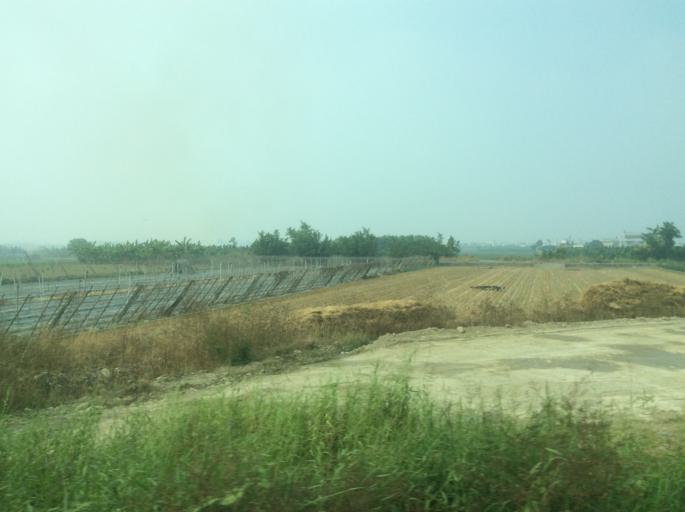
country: TW
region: Taiwan
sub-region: Yunlin
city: Douliu
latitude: 23.7432
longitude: 120.5913
